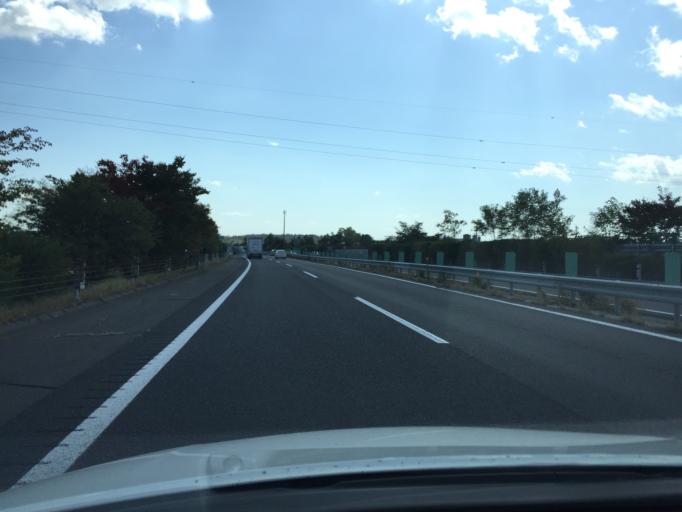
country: JP
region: Fukushima
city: Koriyama
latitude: 37.3636
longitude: 140.3123
